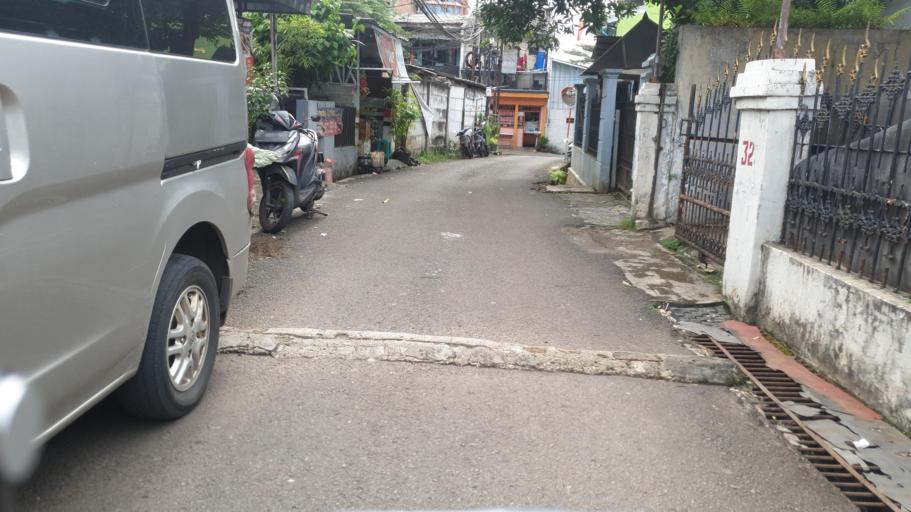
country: ID
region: West Java
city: Pamulang
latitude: -6.2951
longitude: 106.7873
